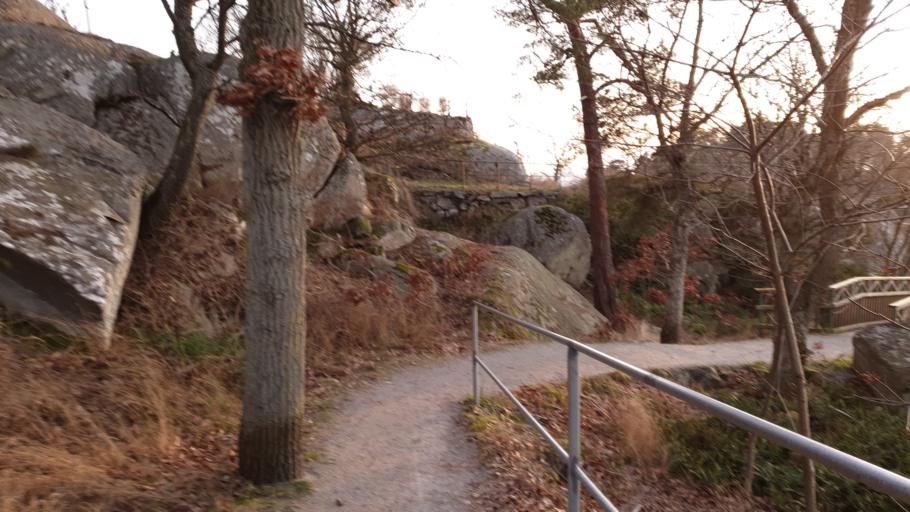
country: SE
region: Blekinge
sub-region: Karlshamns Kommun
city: Karlshamn
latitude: 56.1582
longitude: 14.8785
